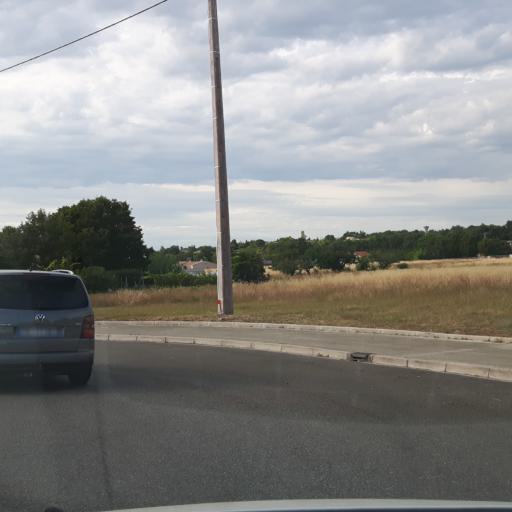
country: FR
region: Midi-Pyrenees
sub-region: Departement de la Haute-Garonne
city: Castelnau-d'Estretefonds
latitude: 43.7759
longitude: 1.3719
